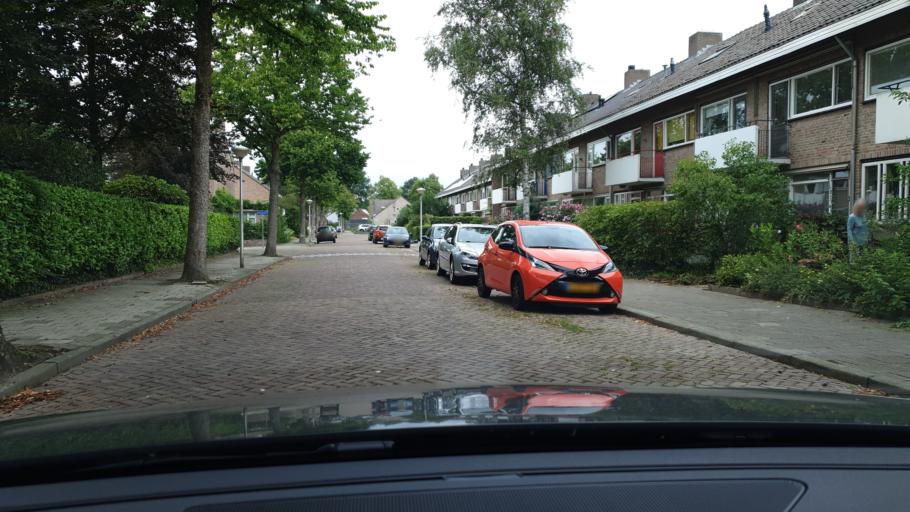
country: NL
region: North Brabant
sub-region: Gemeente Eindhoven
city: Eindhoven
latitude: 51.4672
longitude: 5.4616
